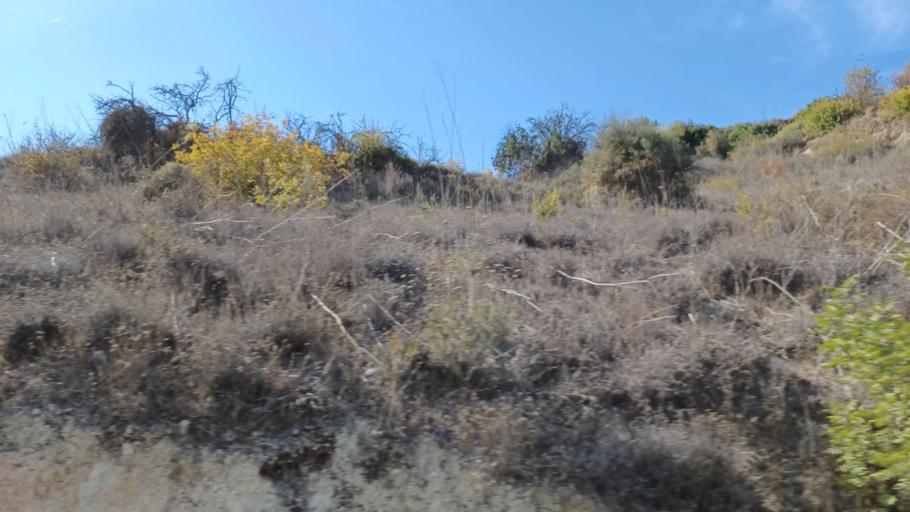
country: CY
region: Pafos
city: Pegeia
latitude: 34.9386
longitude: 32.4532
